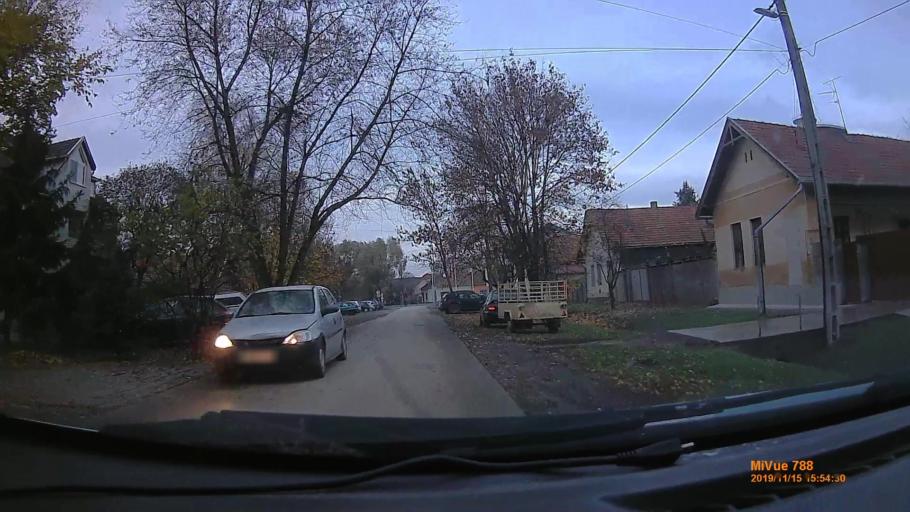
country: HU
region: Bekes
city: Bekescsaba
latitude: 46.6828
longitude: 21.0853
